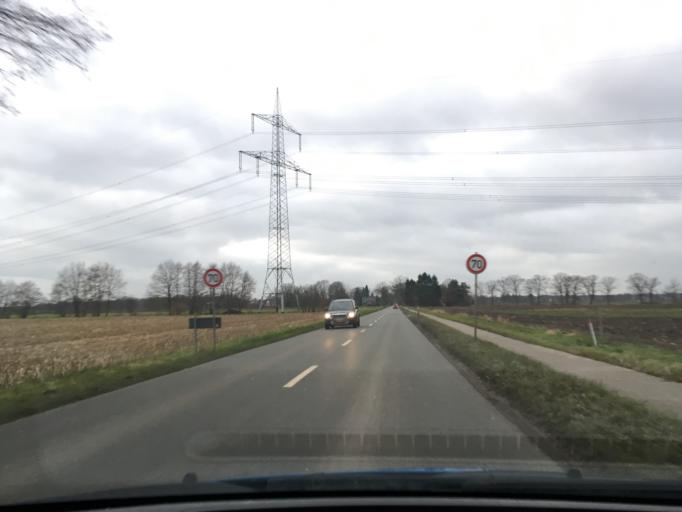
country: DE
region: Lower Saxony
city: Mechtersen
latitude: 53.3059
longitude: 10.3085
